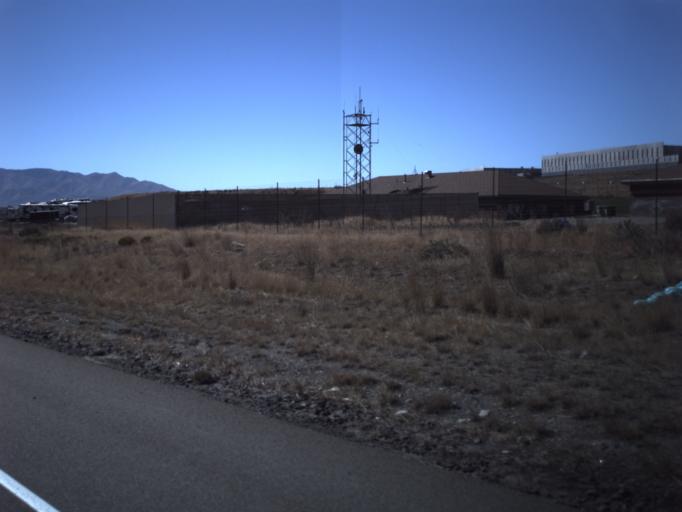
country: US
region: Utah
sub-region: Salt Lake County
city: Bluffdale
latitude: 40.4315
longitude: -111.9285
